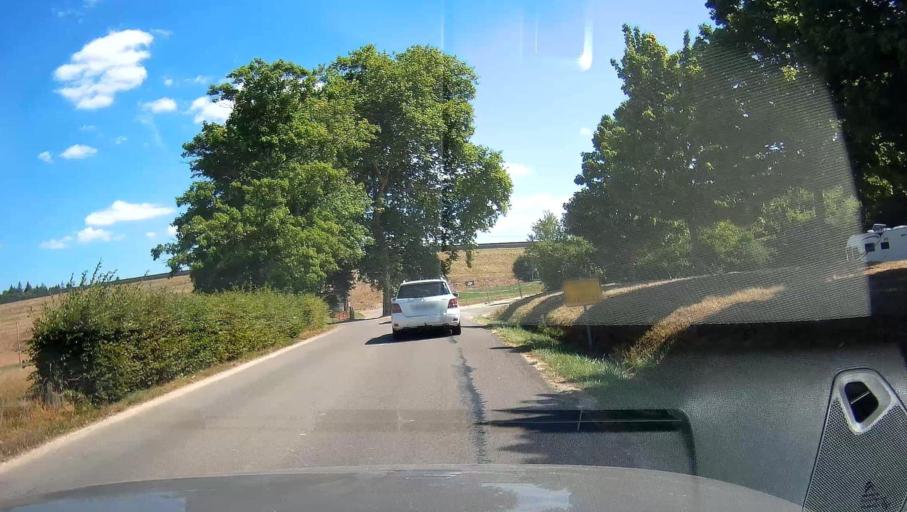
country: FR
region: Champagne-Ardenne
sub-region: Departement de la Haute-Marne
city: Langres
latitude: 47.8647
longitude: 5.3728
